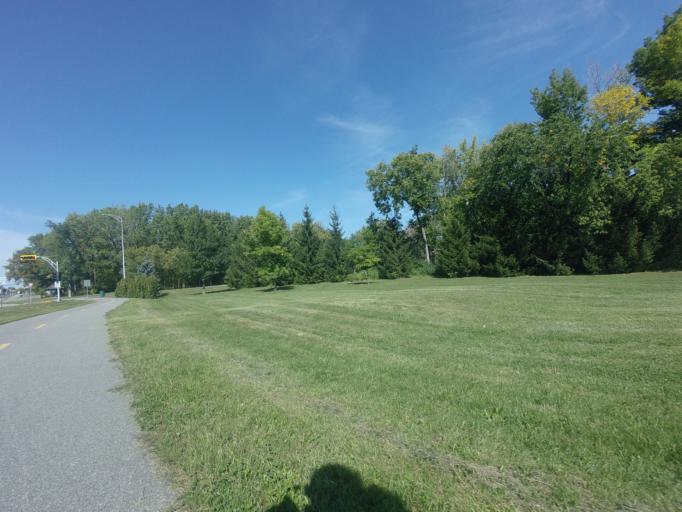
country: CA
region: Quebec
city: Kirkland
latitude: 45.4902
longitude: -73.8708
